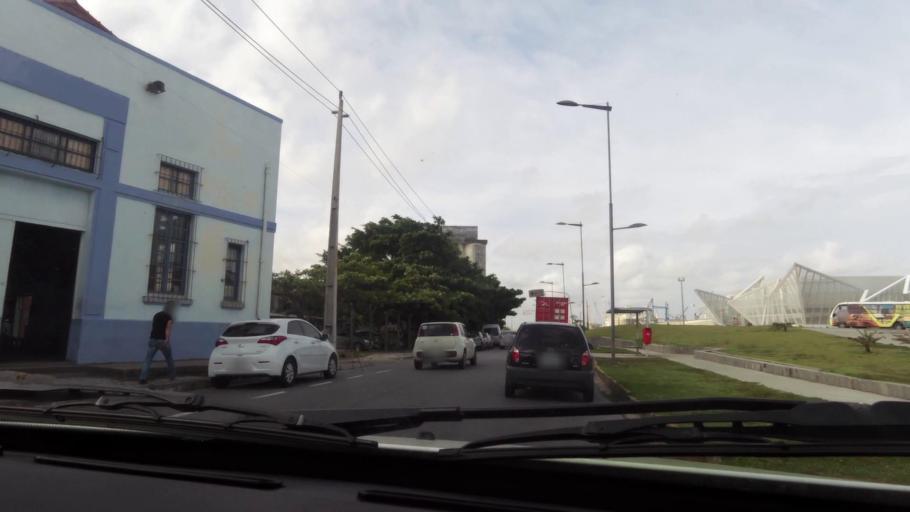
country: BR
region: Pernambuco
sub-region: Recife
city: Recife
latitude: -8.0575
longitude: -34.8697
